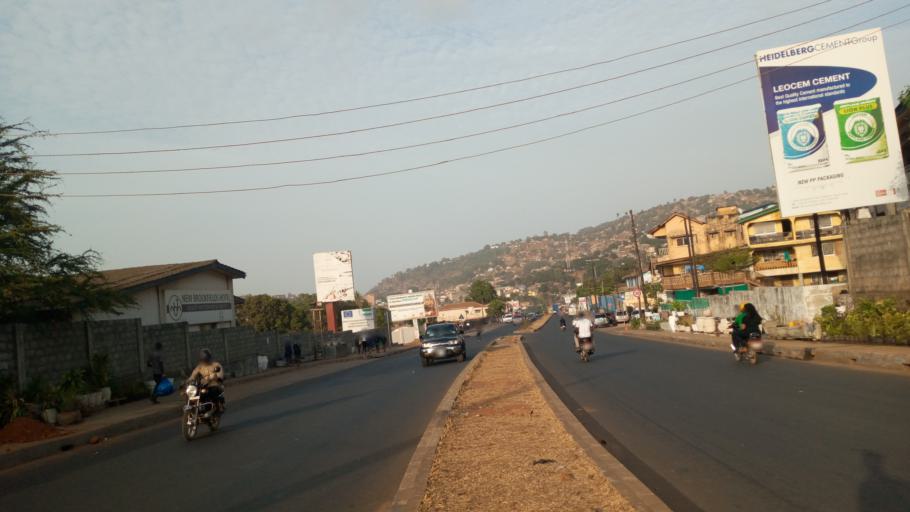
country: SL
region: Western Area
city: Freetown
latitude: 8.4696
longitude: -13.2444
